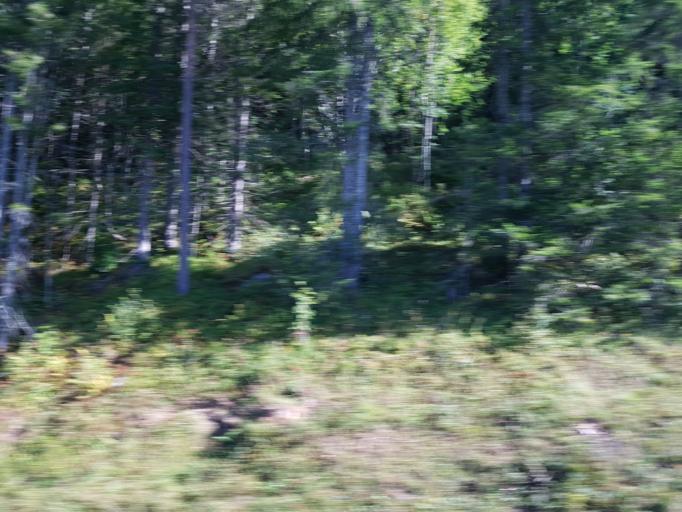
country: NO
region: Sor-Trondelag
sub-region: Afjord
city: A i Afjord
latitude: 63.7571
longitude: 10.2376
